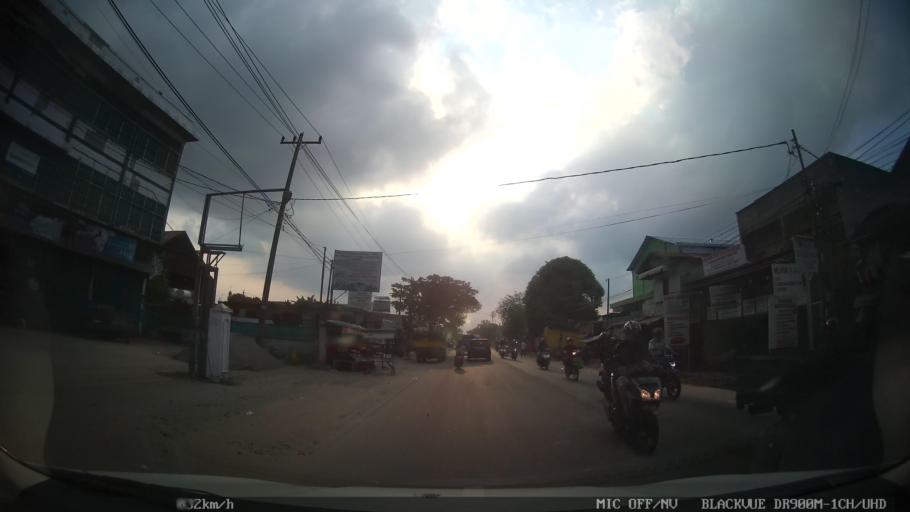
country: ID
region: North Sumatra
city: Medan
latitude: 3.5970
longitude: 98.7351
